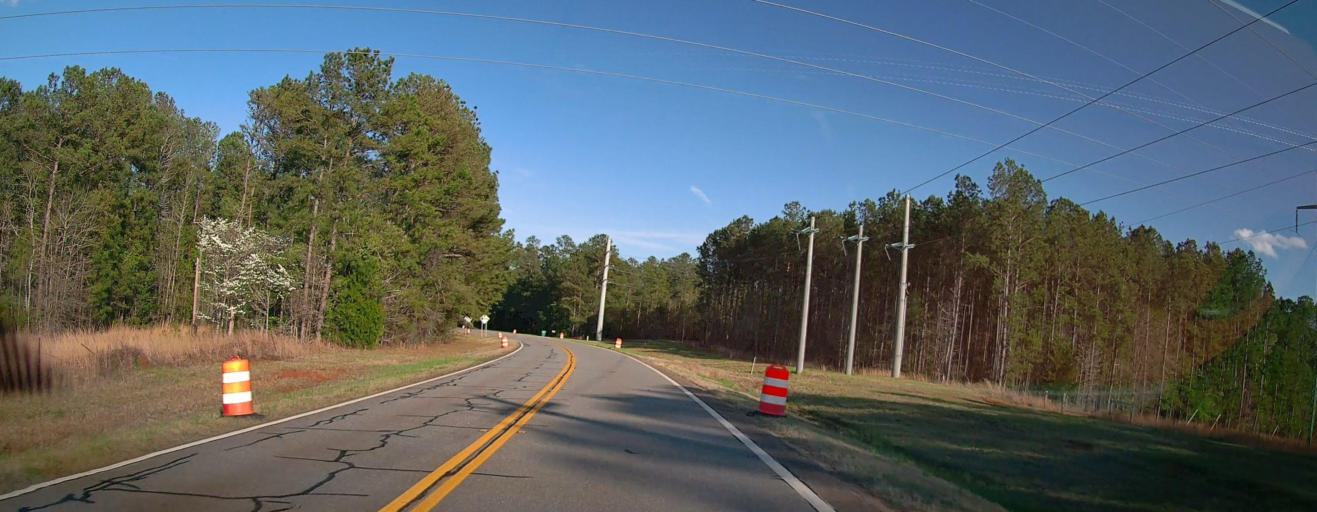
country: US
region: Georgia
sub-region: Baldwin County
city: Milledgeville
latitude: 33.1273
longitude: -83.3152
